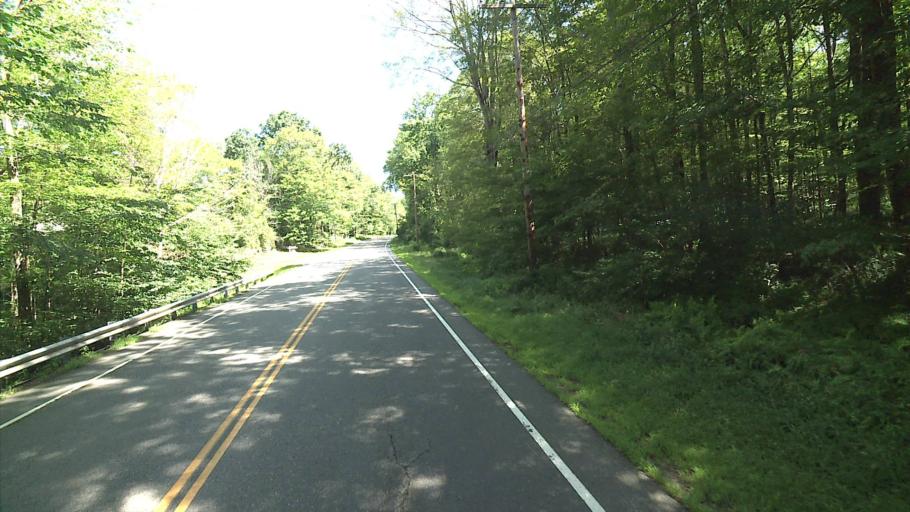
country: US
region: Connecticut
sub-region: Windham County
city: East Brooklyn
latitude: 41.8110
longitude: -72.0455
